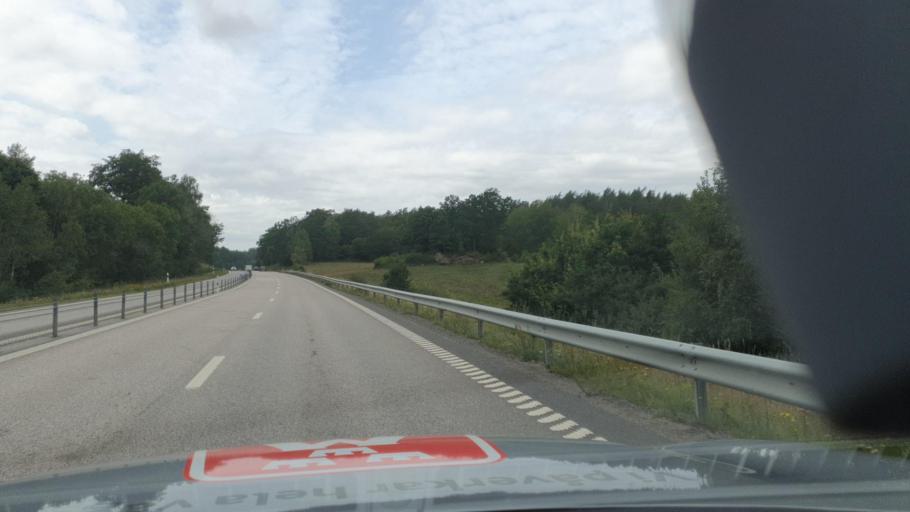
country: SE
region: Blekinge
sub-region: Karlshamns Kommun
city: Karlshamn
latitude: 56.1889
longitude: 14.9223
